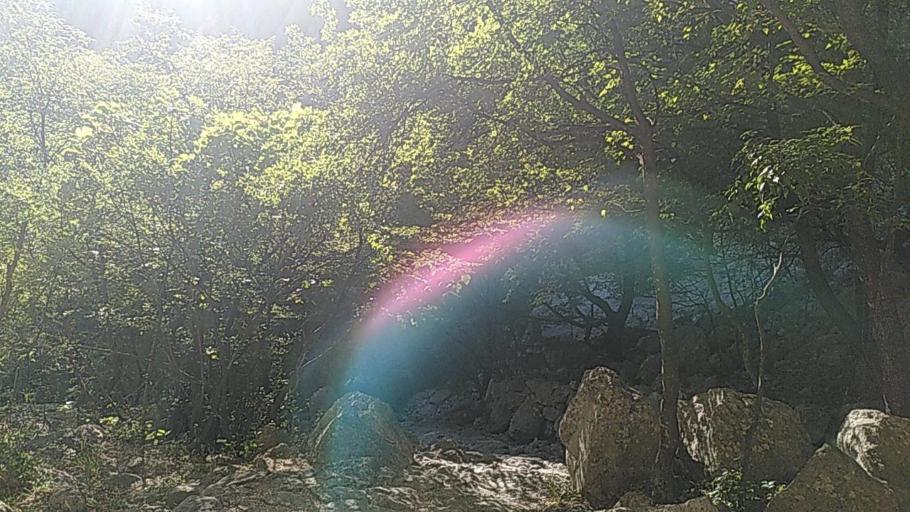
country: HR
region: Zadarska
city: Starigrad
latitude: 44.3074
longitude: 15.4764
